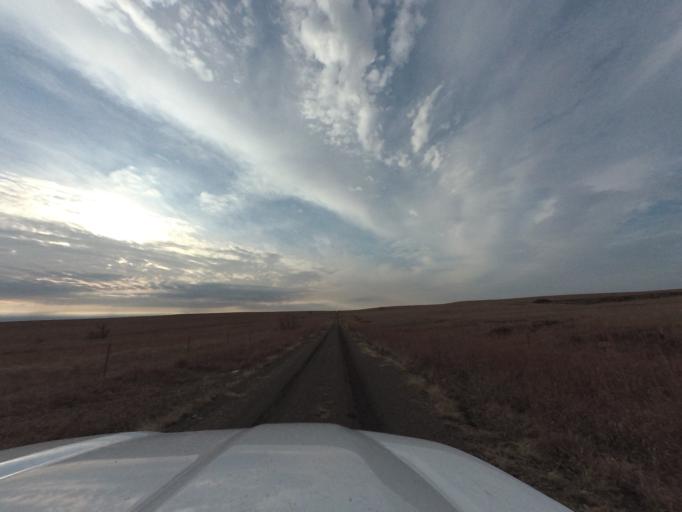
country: US
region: Kansas
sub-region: Chase County
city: Cottonwood Falls
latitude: 38.4672
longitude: -96.4471
